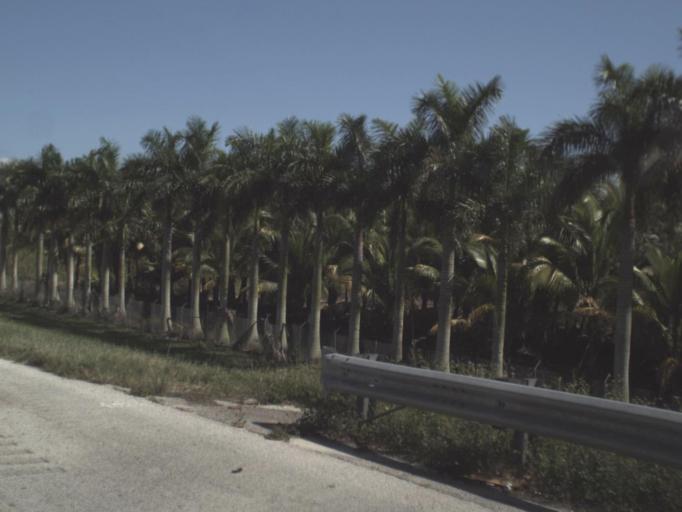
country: US
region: Florida
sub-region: Miami-Dade County
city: Goulds
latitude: 25.5387
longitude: -80.3647
